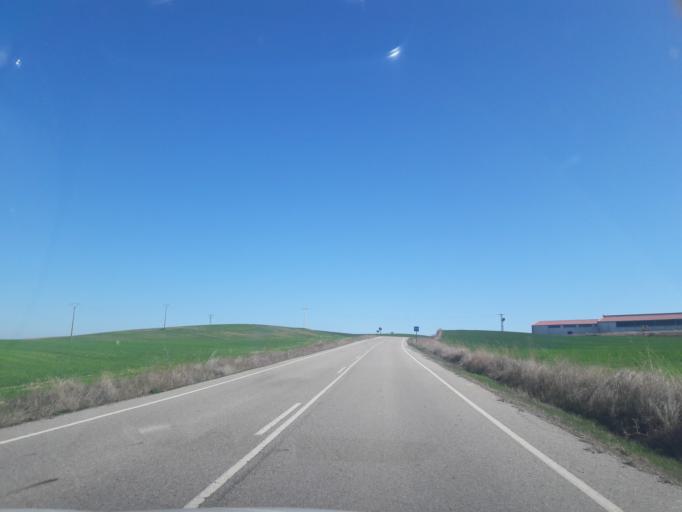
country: ES
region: Castille and Leon
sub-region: Provincia de Salamanca
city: Salmoral
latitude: 40.8126
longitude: -5.2158
